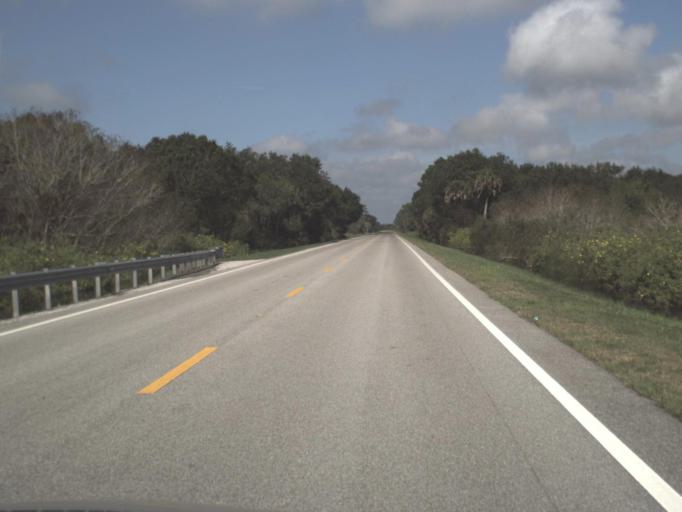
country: US
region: Florida
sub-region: Sarasota County
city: Warm Mineral Springs
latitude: 27.2005
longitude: -82.2338
